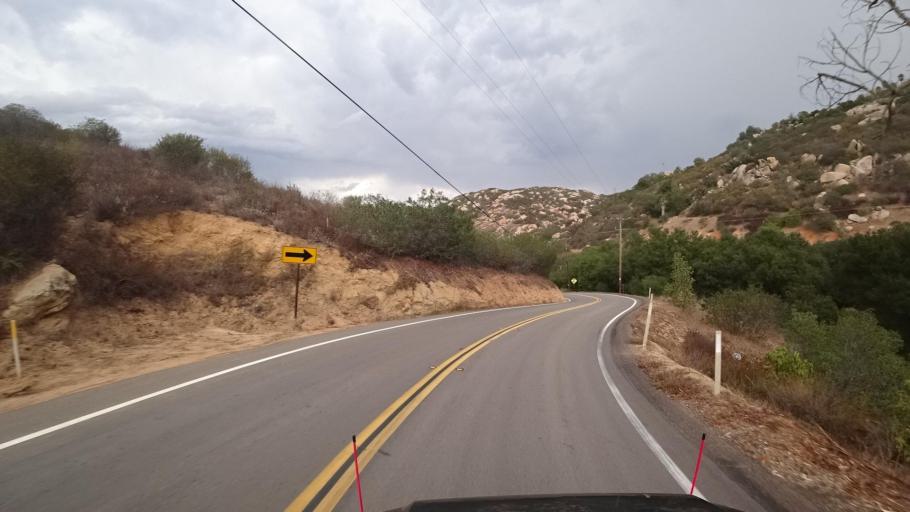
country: US
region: California
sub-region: San Diego County
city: San Pasqual
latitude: 33.0466
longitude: -116.9721
